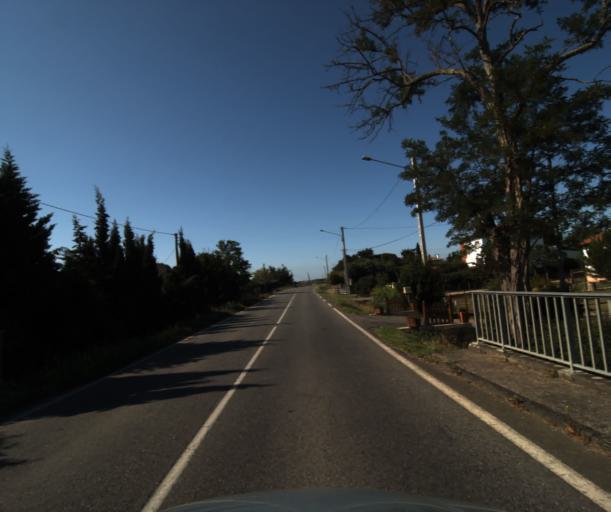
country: FR
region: Midi-Pyrenees
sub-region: Departement de la Haute-Garonne
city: Lagardelle-sur-Leze
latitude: 43.4314
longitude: 1.3786
